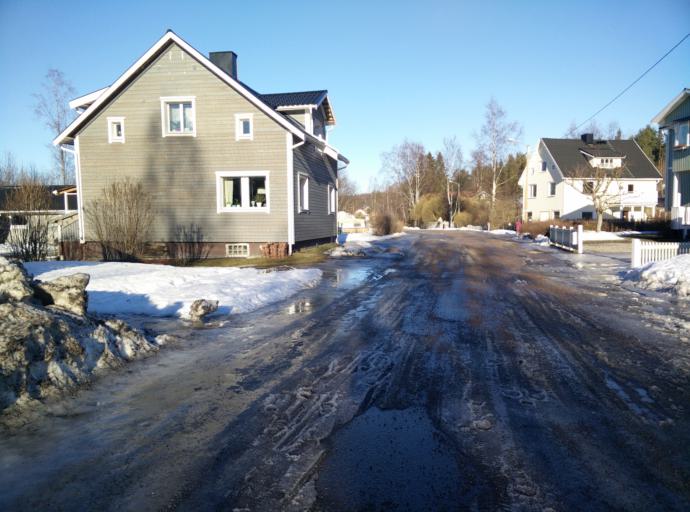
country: SE
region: Vaesternorrland
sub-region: Sundsvalls Kommun
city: Skottsund
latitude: 62.3065
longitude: 17.3872
